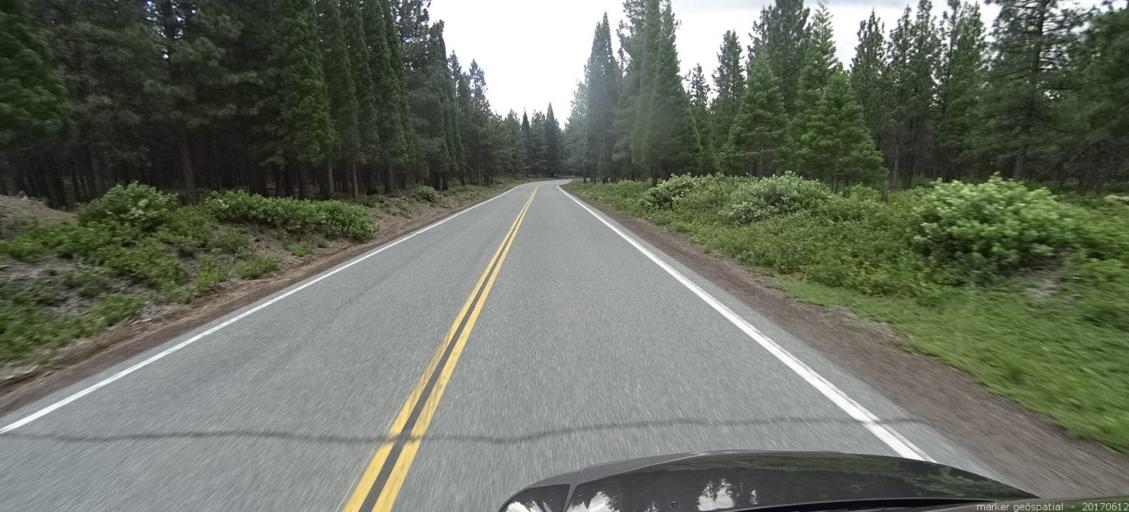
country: US
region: California
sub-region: Siskiyou County
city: Mount Shasta
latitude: 41.3441
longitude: -122.3127
